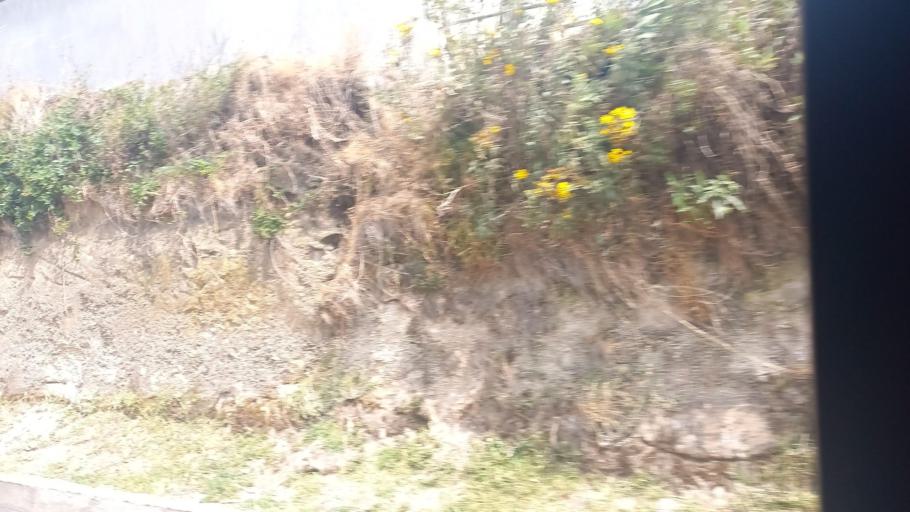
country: EC
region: Pichincha
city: Cayambe
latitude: 0.1576
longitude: -78.0722
